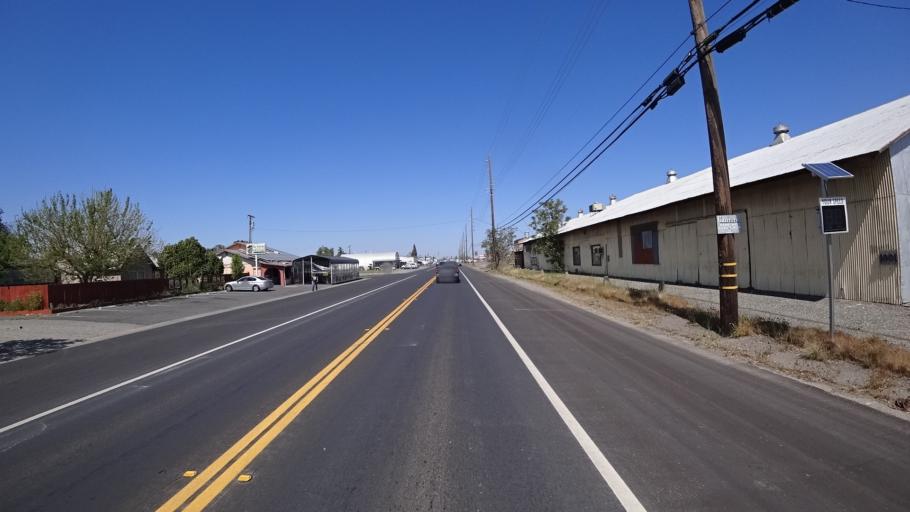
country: US
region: California
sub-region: Glenn County
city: Orland
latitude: 39.7435
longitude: -122.1976
